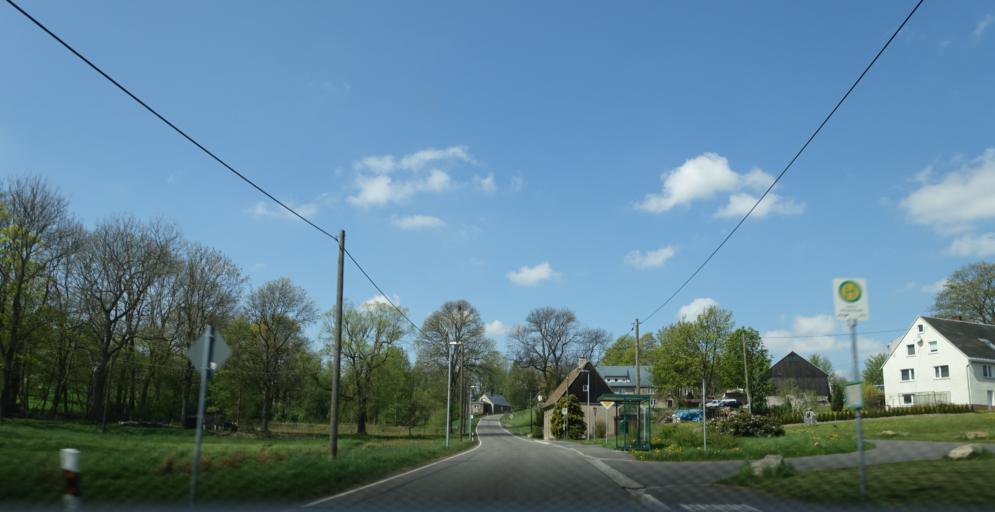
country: DE
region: Saxony
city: Grosshartmannsdorf
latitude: 50.7670
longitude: 13.3594
